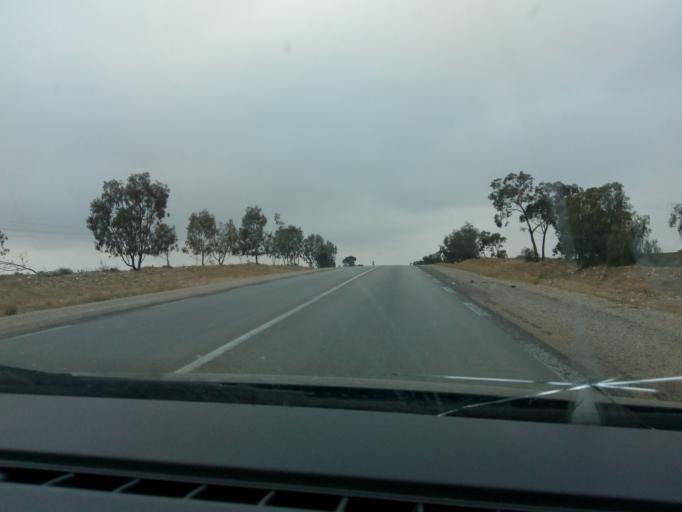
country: TN
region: Madanin
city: Medenine
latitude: 33.2673
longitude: 10.4665
